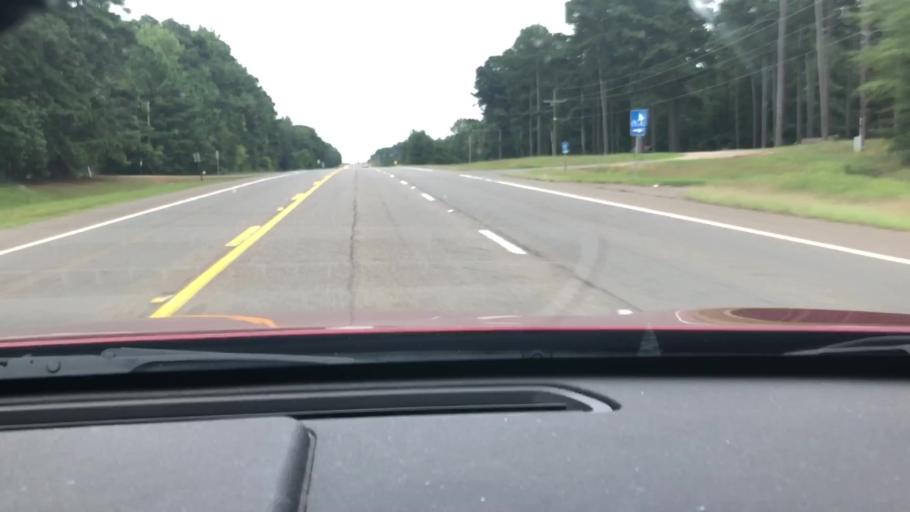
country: US
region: Arkansas
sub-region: Lafayette County
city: Stamps
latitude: 33.3637
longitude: -93.4689
